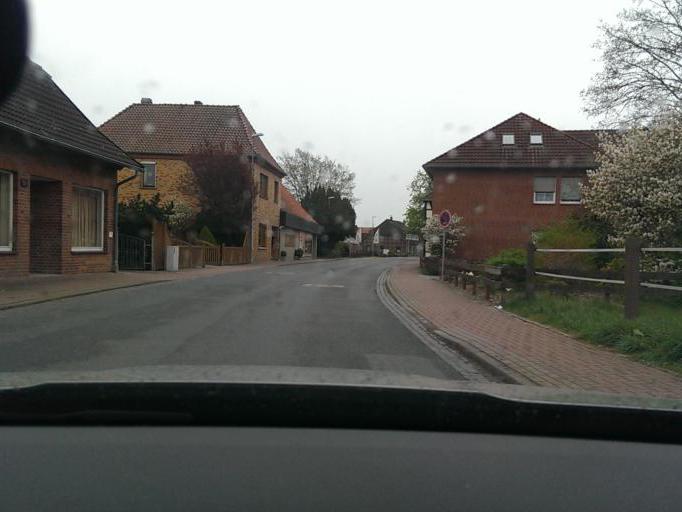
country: DE
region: Lower Saxony
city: Steimbke
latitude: 52.6555
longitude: 9.4853
